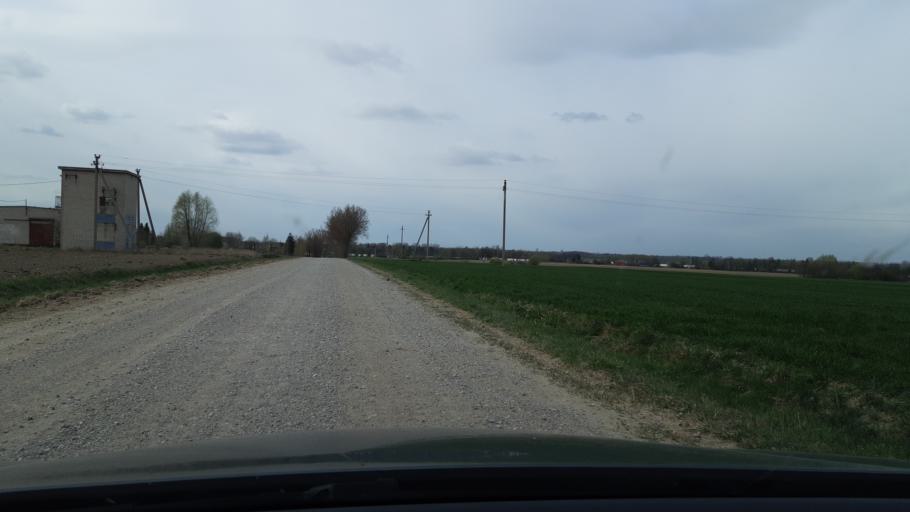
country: LT
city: Virbalis
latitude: 54.6166
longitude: 22.8422
